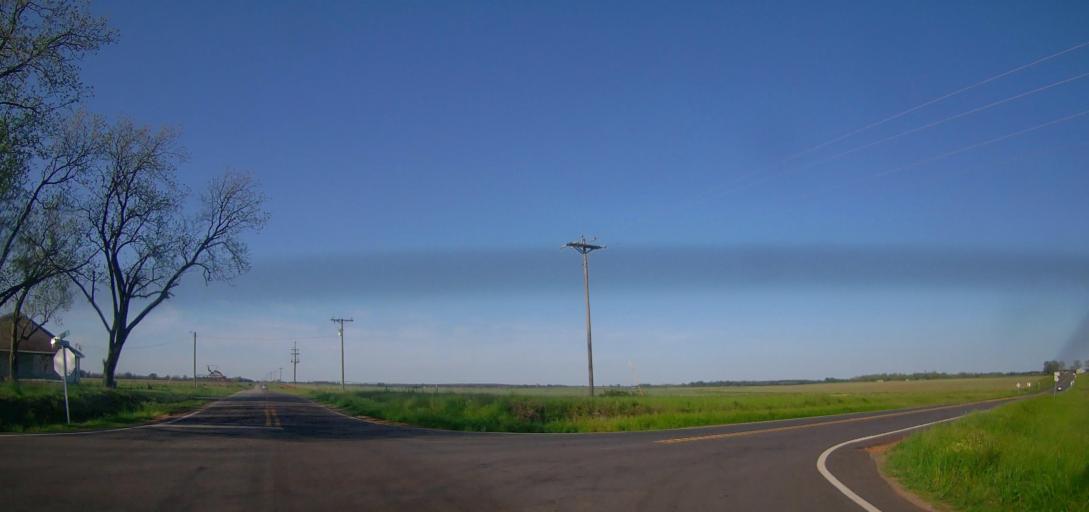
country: US
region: Georgia
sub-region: Macon County
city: Marshallville
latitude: 32.3586
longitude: -83.9407
